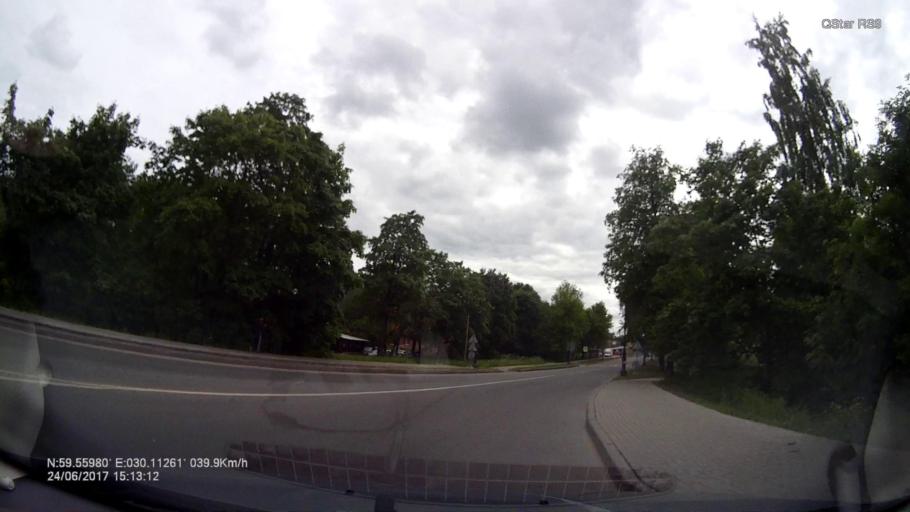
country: RU
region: Leningrad
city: Gatchina
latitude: 59.5596
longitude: 30.1126
